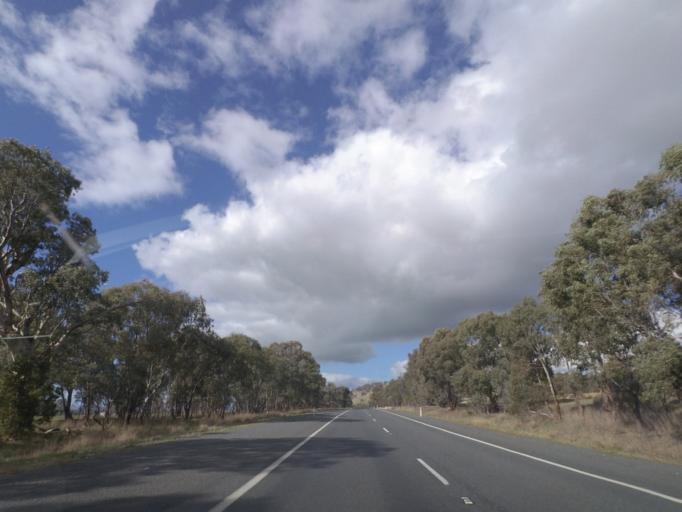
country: AU
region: New South Wales
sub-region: Greater Hume Shire
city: Holbrook
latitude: -35.6732
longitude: 147.3871
